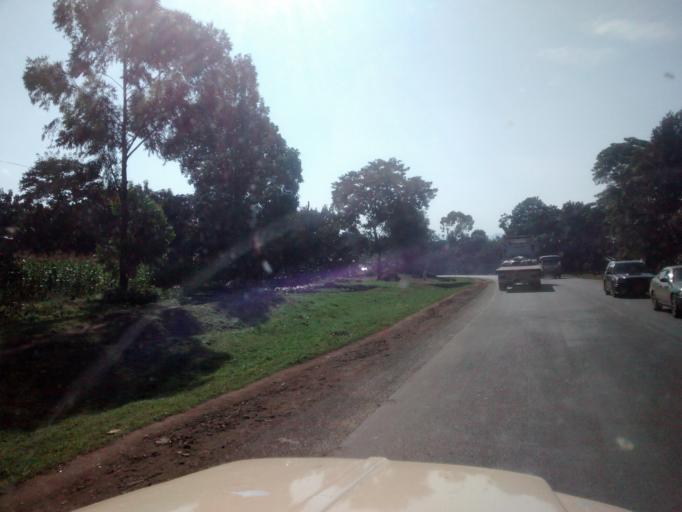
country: TZ
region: Arusha
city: Nkoaranga
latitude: -3.3727
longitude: 36.7894
